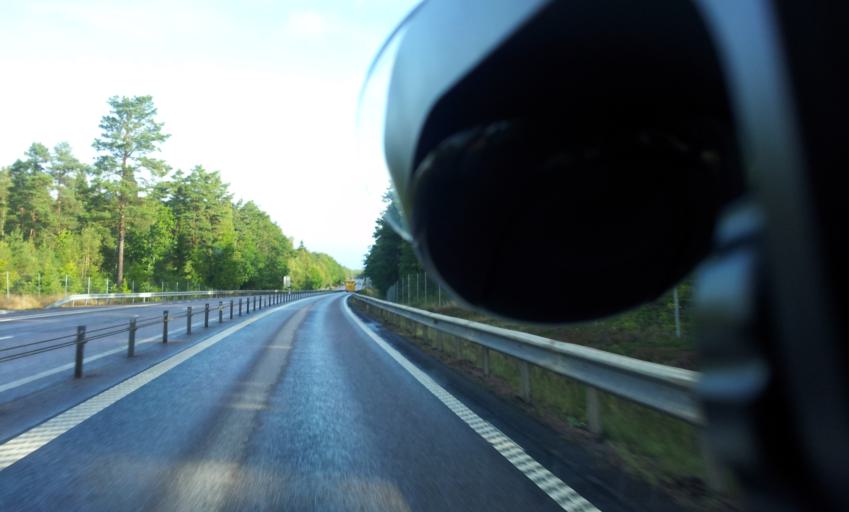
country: SE
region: Kalmar
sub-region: Oskarshamns Kommun
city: Paskallavik
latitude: 57.1663
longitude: 16.4440
